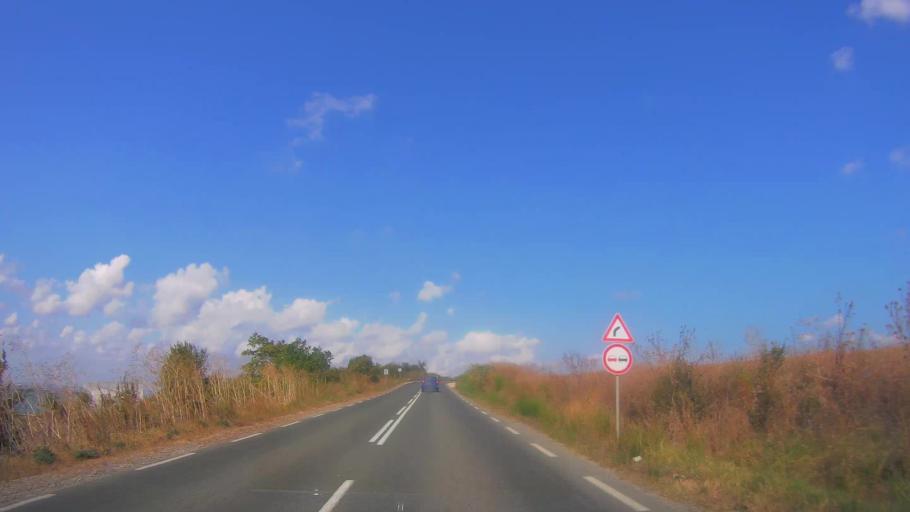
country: BG
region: Burgas
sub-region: Obshtina Burgas
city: Burgas
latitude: 42.4791
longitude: 27.3724
